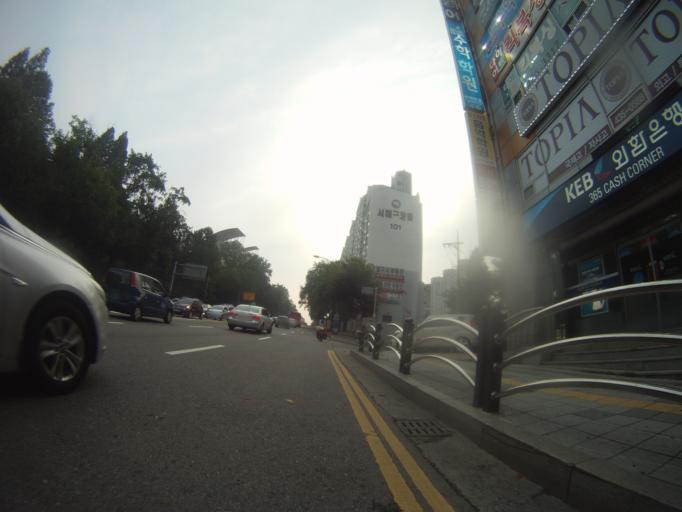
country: KR
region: Incheon
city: Incheon
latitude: 37.4568
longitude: 126.7025
